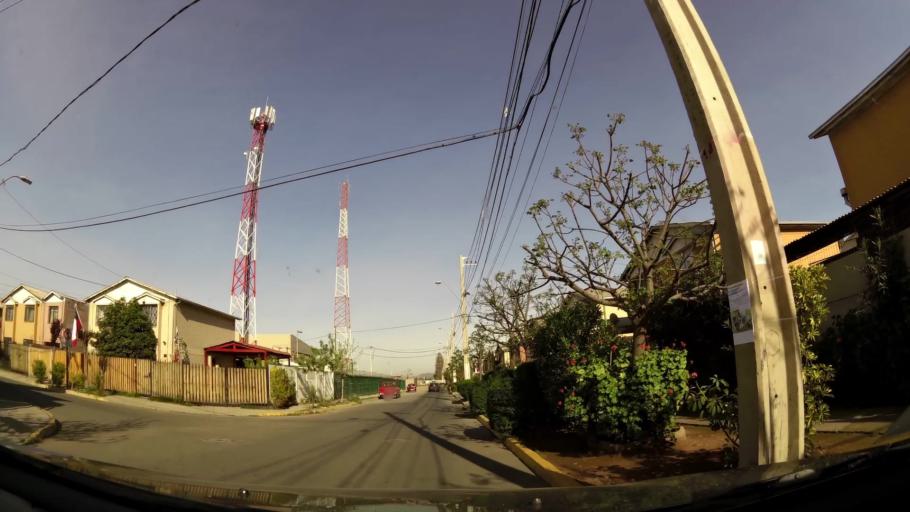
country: CL
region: Santiago Metropolitan
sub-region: Provincia de Cordillera
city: Puente Alto
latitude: -33.6128
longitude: -70.5970
